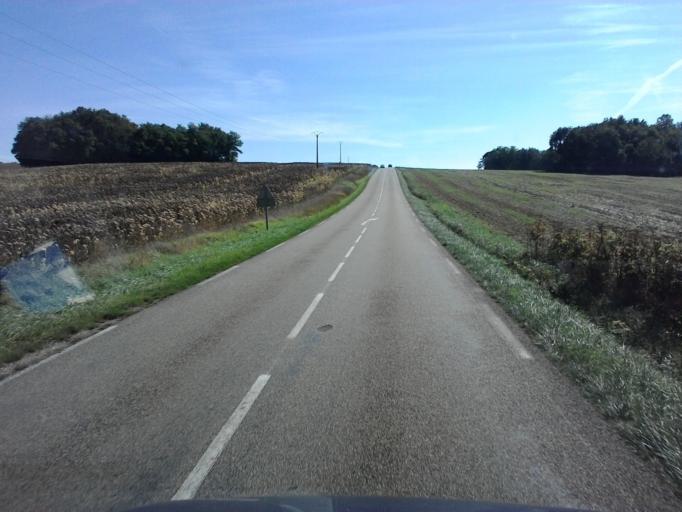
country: FR
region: Bourgogne
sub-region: Departement de l'Yonne
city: Joux-la-Ville
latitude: 47.5773
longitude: 3.8778
